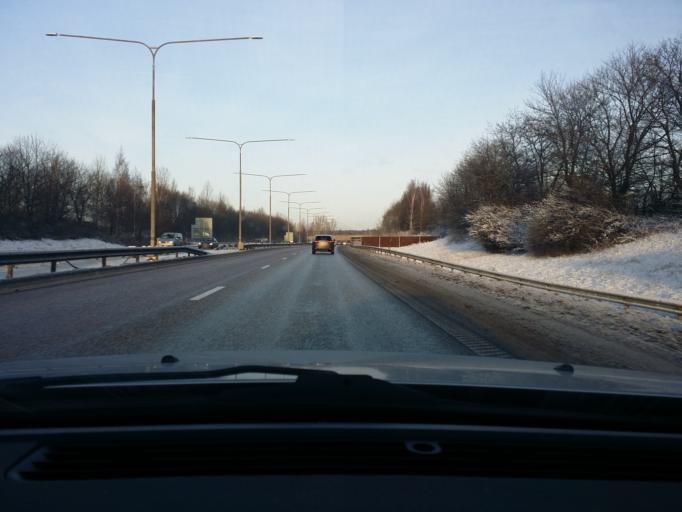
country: SE
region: OErebro
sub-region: Orebro Kommun
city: Orebro
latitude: 59.2803
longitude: 15.1809
